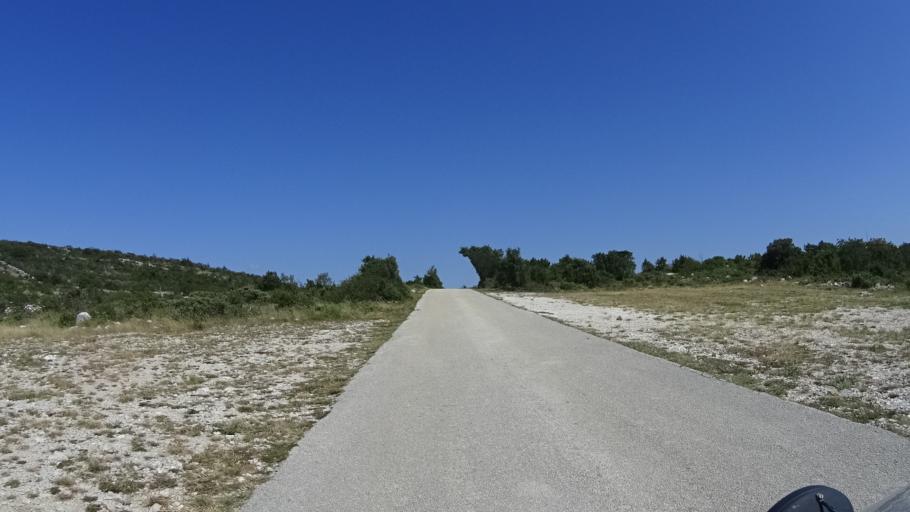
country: HR
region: Istarska
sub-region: Grad Labin
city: Rabac
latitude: 44.9790
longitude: 14.1451
